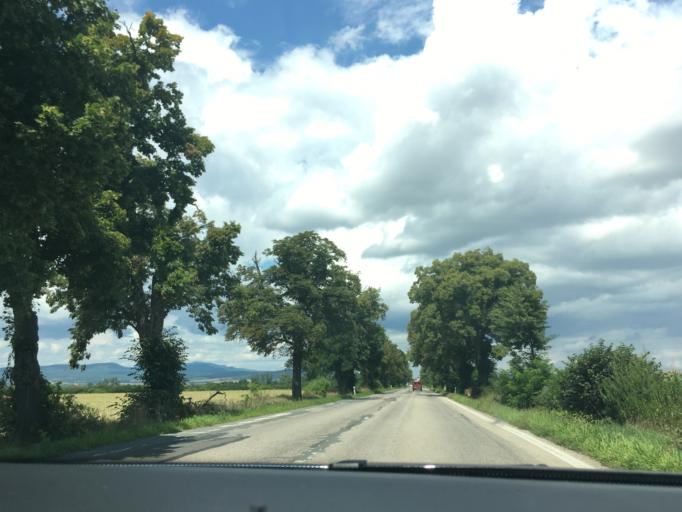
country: HU
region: Borsod-Abauj-Zemplen
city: Satoraljaujhely
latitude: 48.4522
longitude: 21.6487
